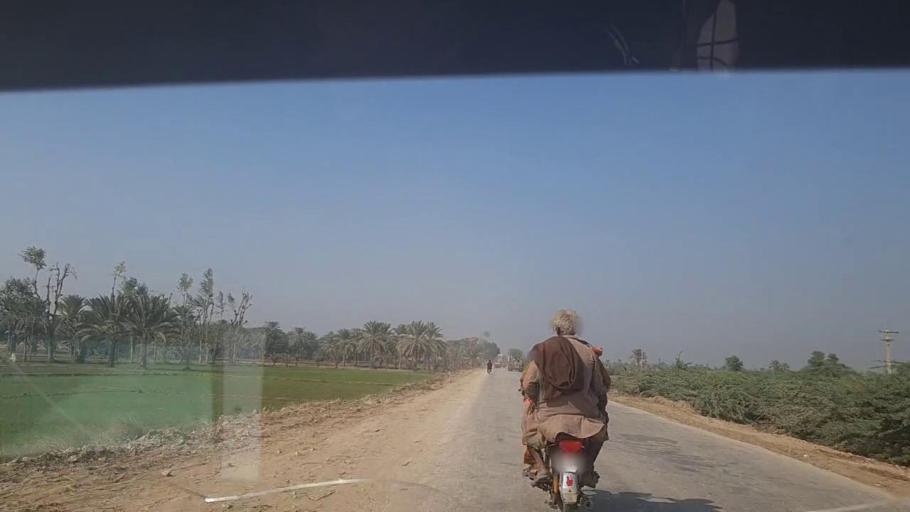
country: PK
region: Sindh
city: Kot Diji
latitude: 27.4163
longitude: 68.6640
